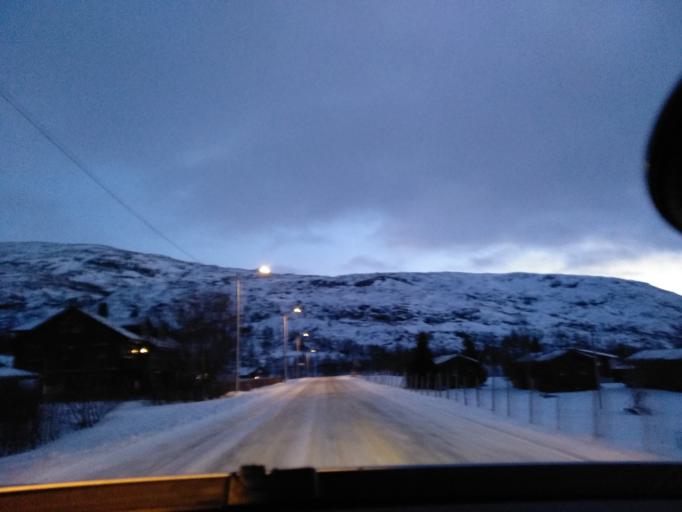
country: NO
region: Vest-Agder
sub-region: Sirdal
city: Tonstad
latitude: 59.0150
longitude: 6.9380
